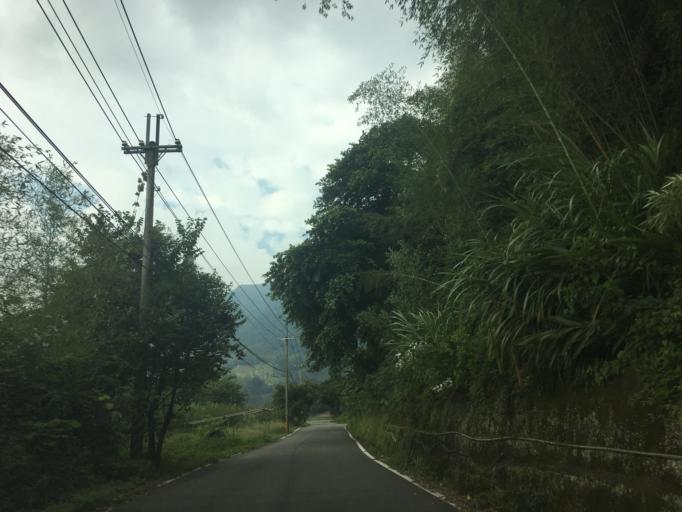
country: TW
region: Taiwan
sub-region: Miaoli
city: Miaoli
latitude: 24.3510
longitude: 120.9453
